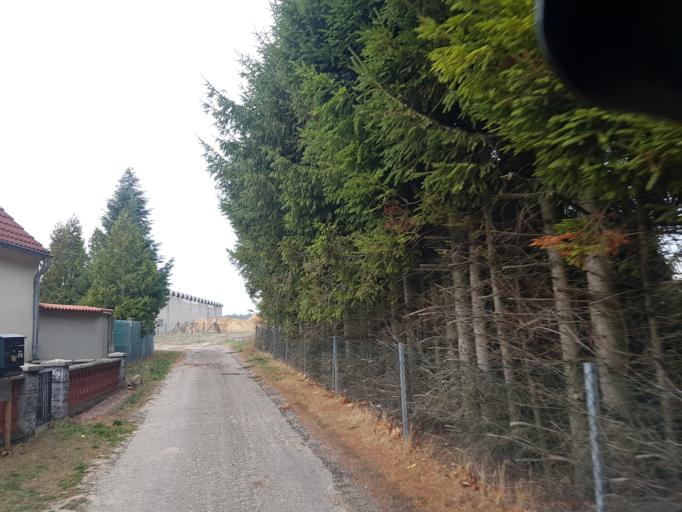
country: DE
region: Brandenburg
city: Treuenbrietzen
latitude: 52.0388
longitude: 12.8059
